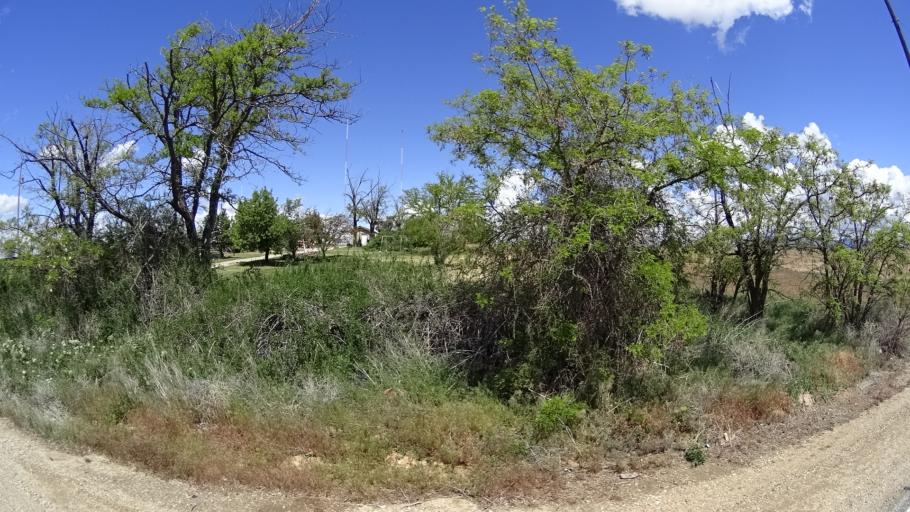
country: US
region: Idaho
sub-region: Ada County
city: Kuna
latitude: 43.5465
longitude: -116.4106
